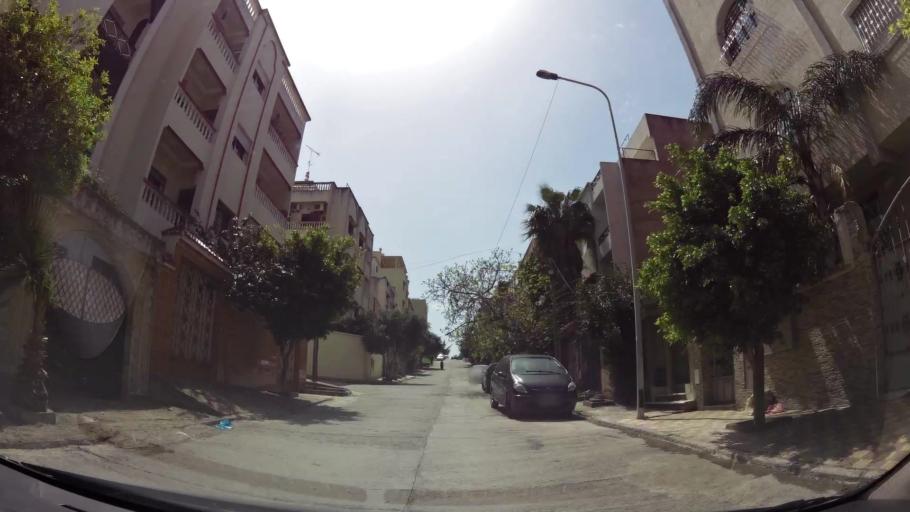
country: MA
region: Tanger-Tetouan
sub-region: Tanger-Assilah
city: Tangier
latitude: 35.7593
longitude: -5.8347
